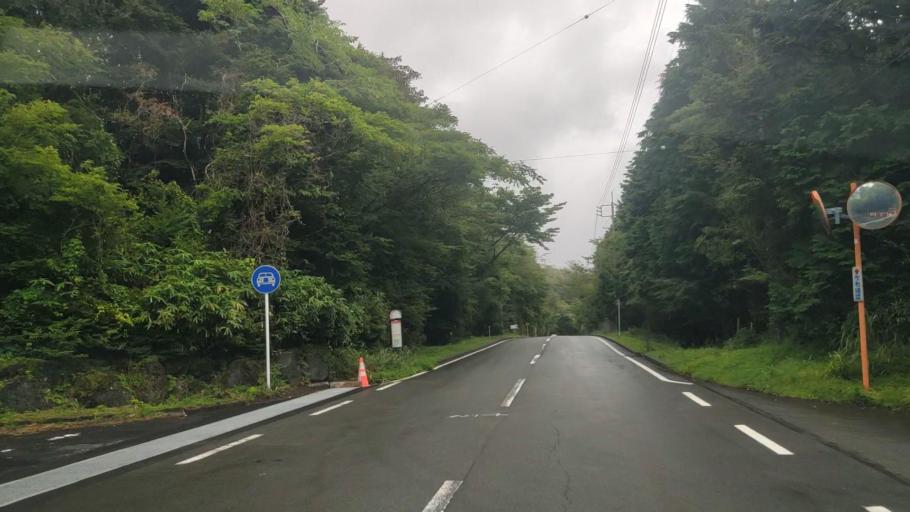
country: JP
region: Shizuoka
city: Gotemba
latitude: 35.2813
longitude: 138.7880
